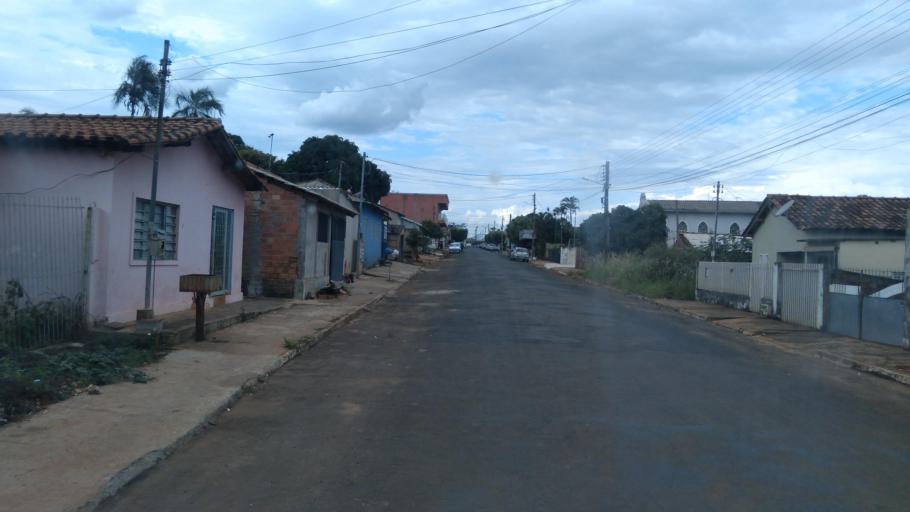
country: BR
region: Goias
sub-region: Mineiros
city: Mineiros
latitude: -17.5722
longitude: -52.5626
